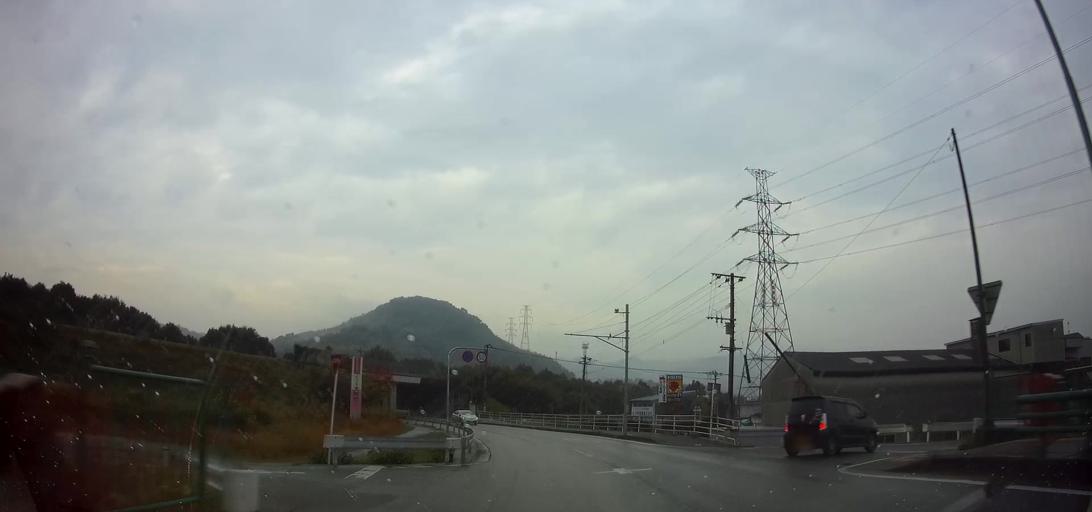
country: JP
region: Nagasaki
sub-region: Isahaya-shi
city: Isahaya
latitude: 32.8488
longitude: 130.0108
